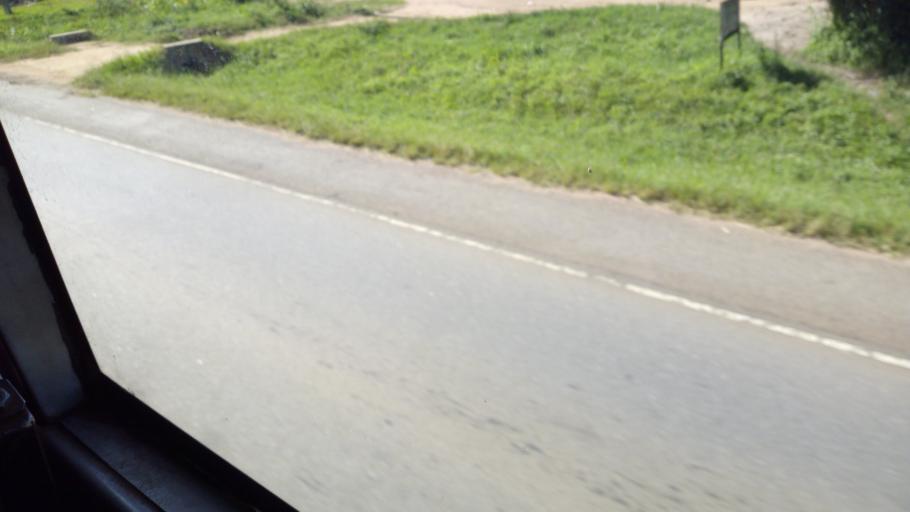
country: UG
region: Central Region
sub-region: Lyantonde District
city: Lyantonde
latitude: -0.4306
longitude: 31.0998
